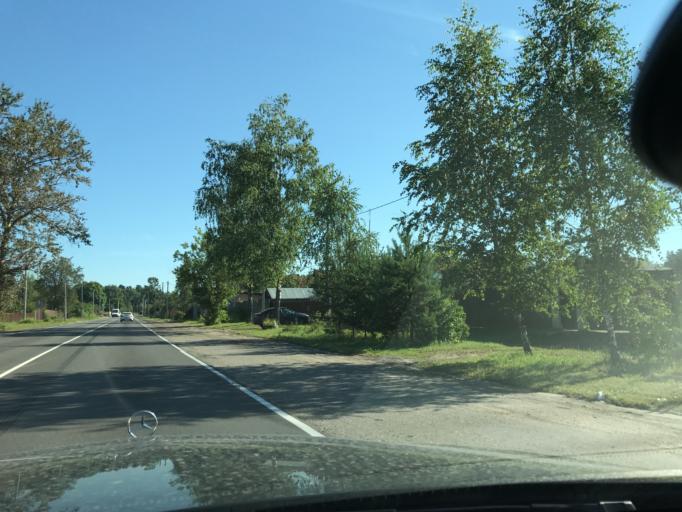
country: RU
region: Moskovskaya
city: Noginsk-9
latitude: 56.0661
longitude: 38.5578
